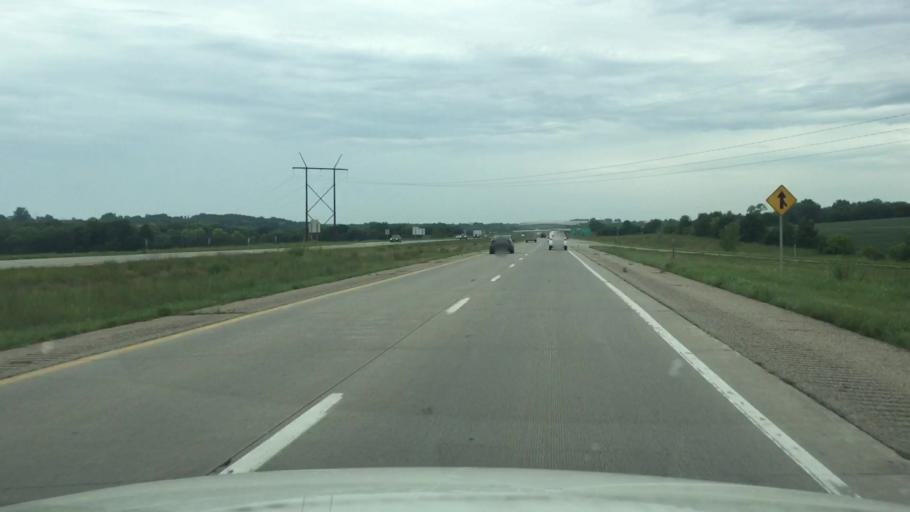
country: US
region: Iowa
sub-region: Warren County
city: Norwalk
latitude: 41.5004
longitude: -93.6294
